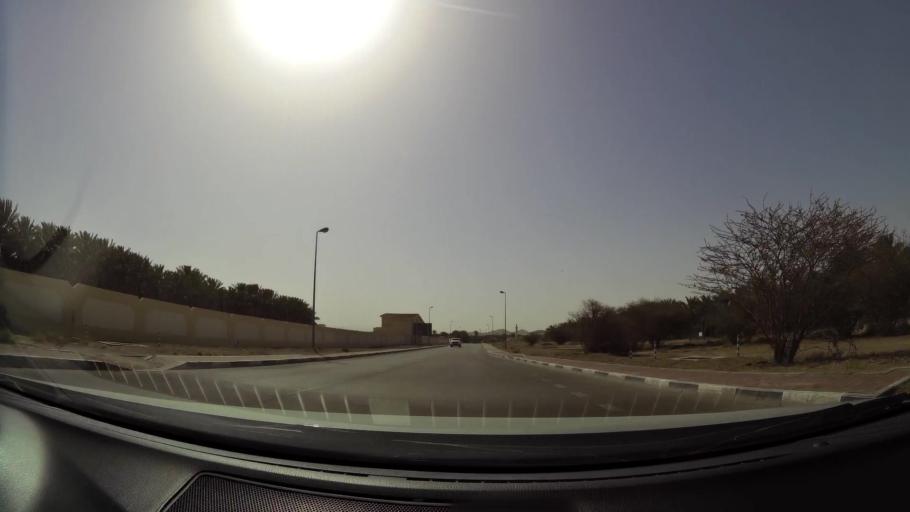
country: OM
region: Al Buraimi
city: Al Buraymi
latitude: 24.3150
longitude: 55.7980
